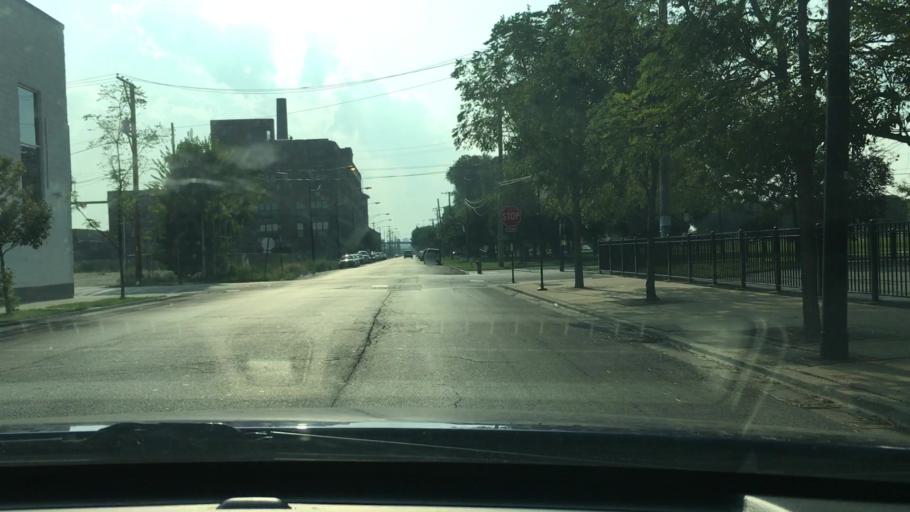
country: US
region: Illinois
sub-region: Cook County
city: Chicago
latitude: 41.8616
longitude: -87.6609
